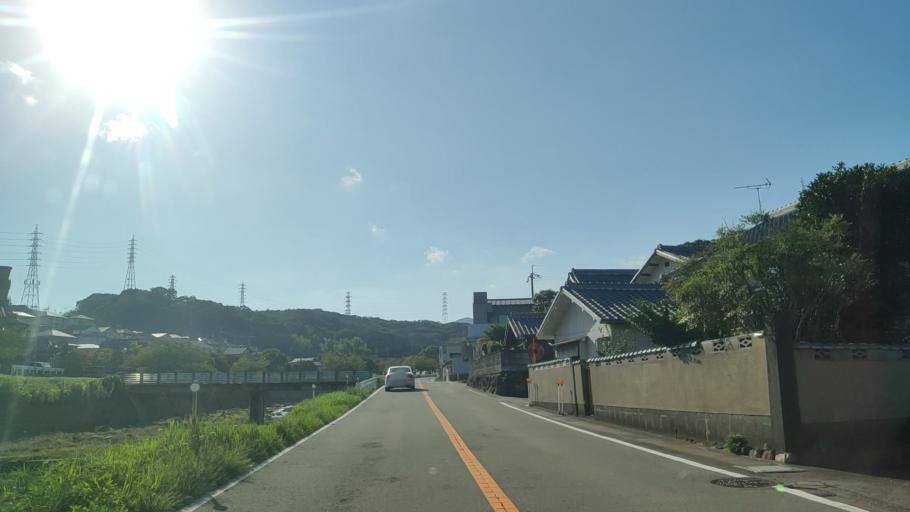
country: JP
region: Hyogo
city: Sandacho
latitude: 34.8240
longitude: 135.2451
